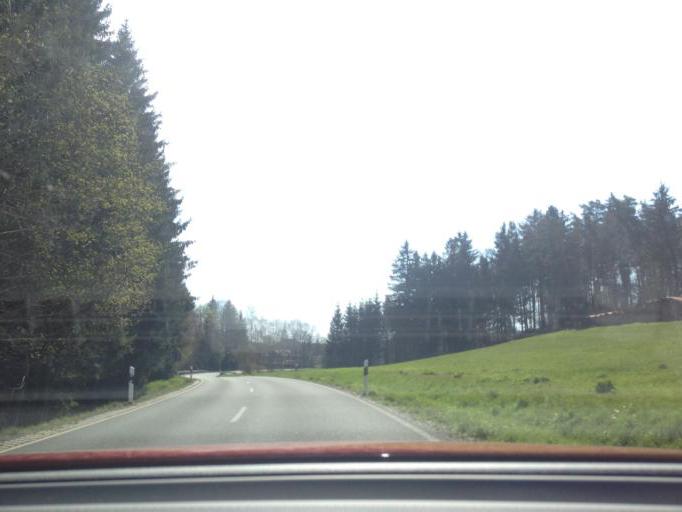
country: DE
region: Bavaria
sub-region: Upper Franconia
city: Oberhaid
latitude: 50.0982
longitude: 11.7841
